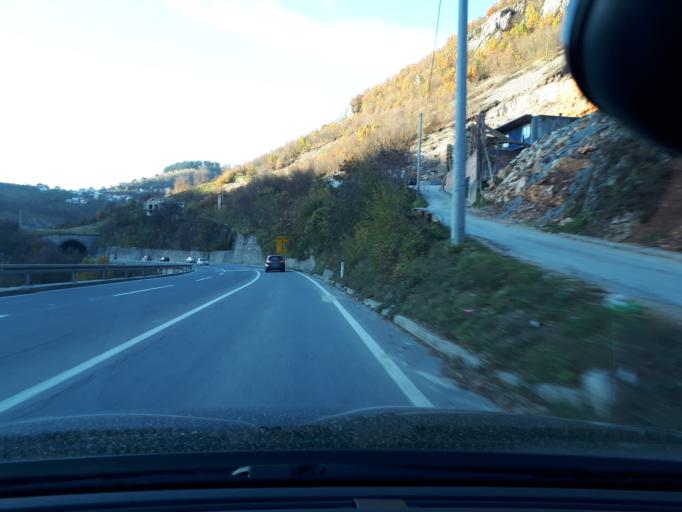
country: BA
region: Federation of Bosnia and Herzegovina
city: Kobilja Glava
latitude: 43.8551
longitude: 18.4585
